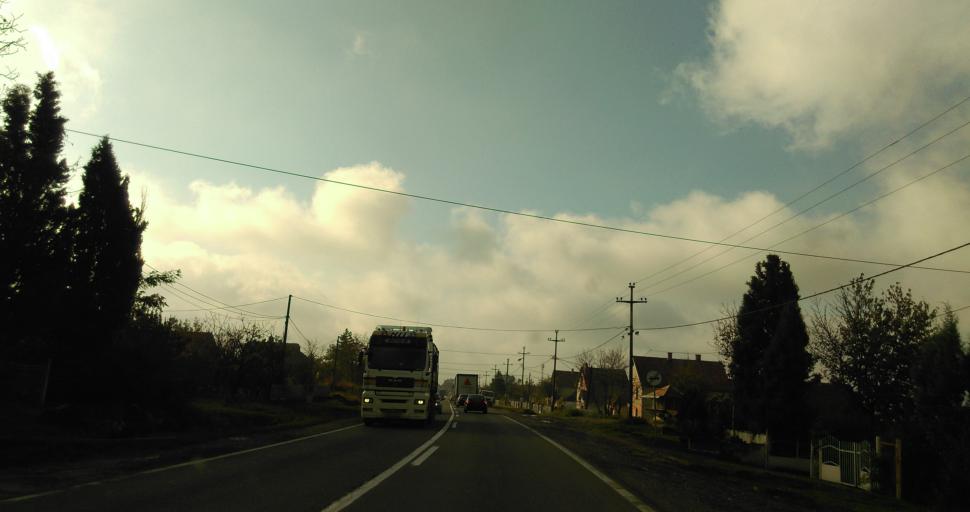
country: RS
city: Stepojevac
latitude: 44.5270
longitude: 20.2934
